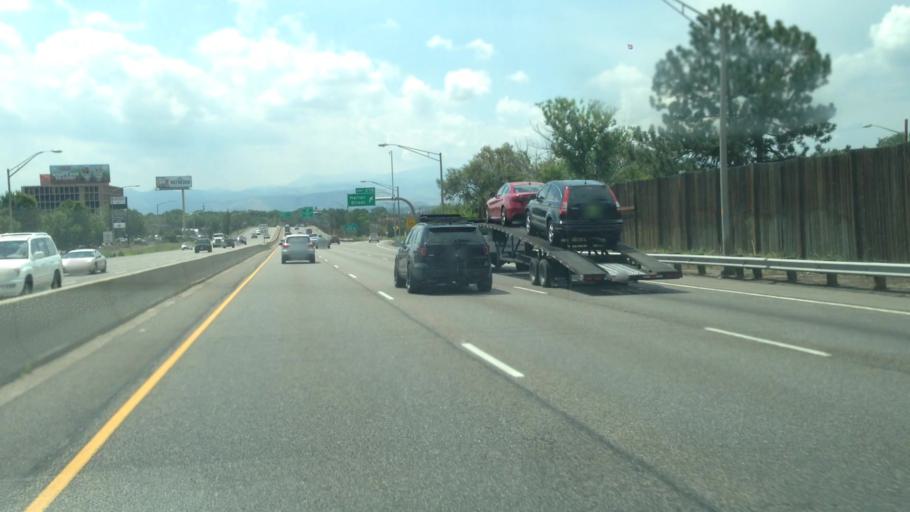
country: US
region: Colorado
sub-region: Jefferson County
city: Wheat Ridge
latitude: 39.7837
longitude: -105.0565
